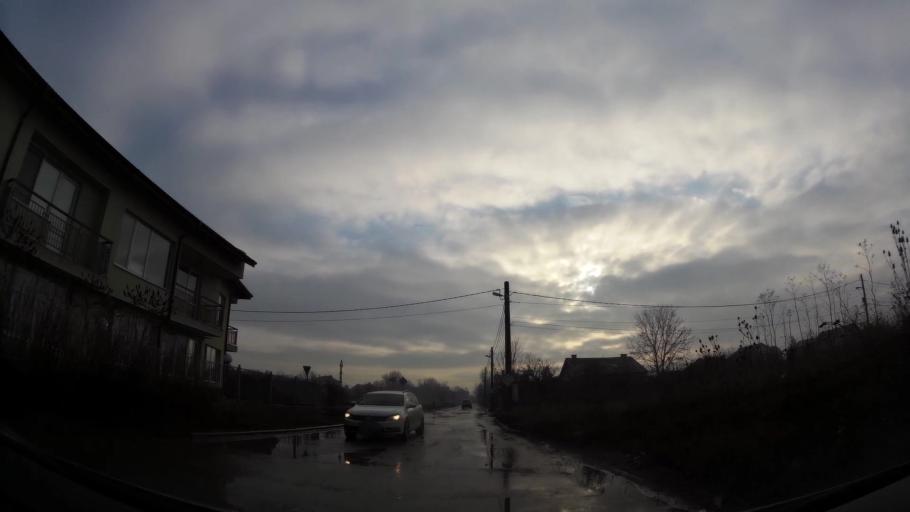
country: BG
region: Sofia-Capital
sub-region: Stolichna Obshtina
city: Sofia
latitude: 42.7379
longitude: 23.3361
